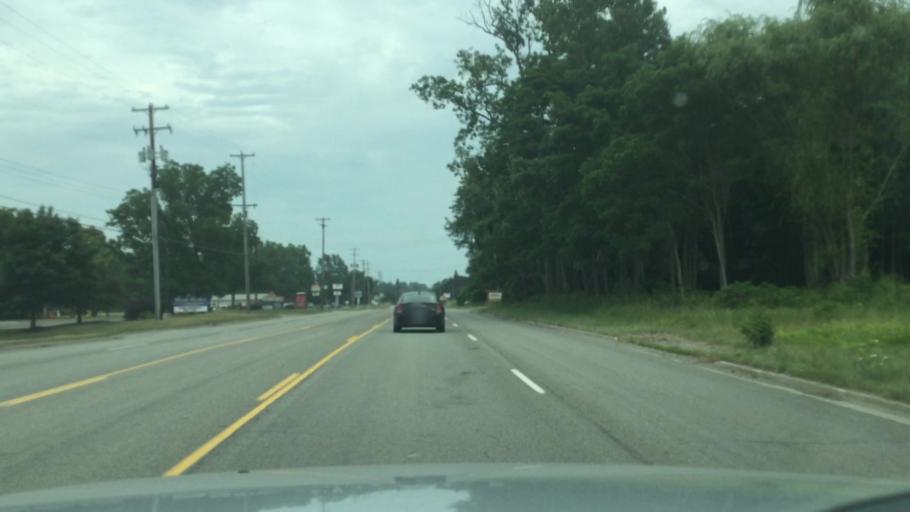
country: US
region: Michigan
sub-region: Genesee County
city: Flint
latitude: 42.9442
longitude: -83.7091
